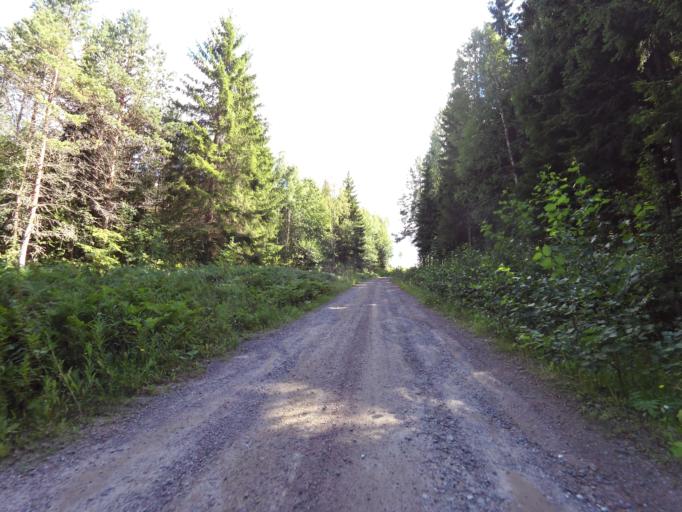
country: SE
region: Gaevleborg
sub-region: Hofors Kommun
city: Hofors
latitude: 60.5304
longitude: 16.2313
